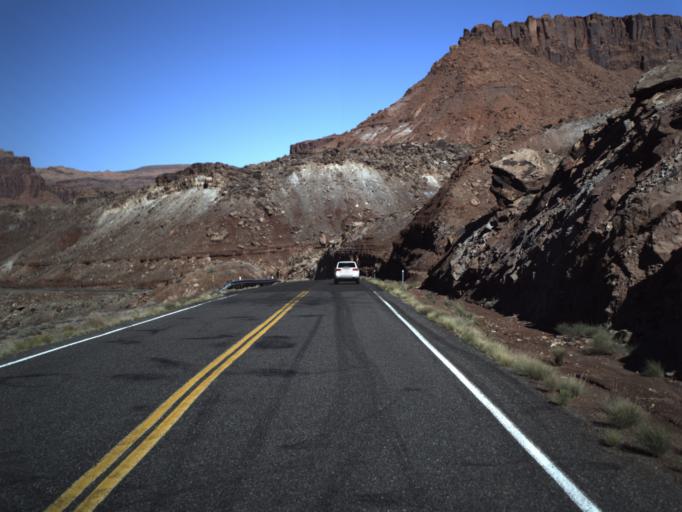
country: US
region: Utah
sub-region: San Juan County
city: Blanding
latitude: 37.8902
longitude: -110.4338
